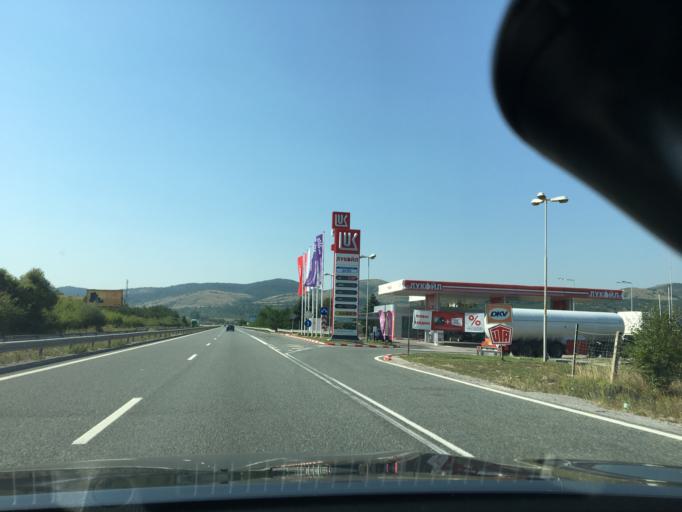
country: BG
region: Pernik
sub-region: Obshtina Pernik
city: Pernik
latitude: 42.5715
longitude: 23.1167
